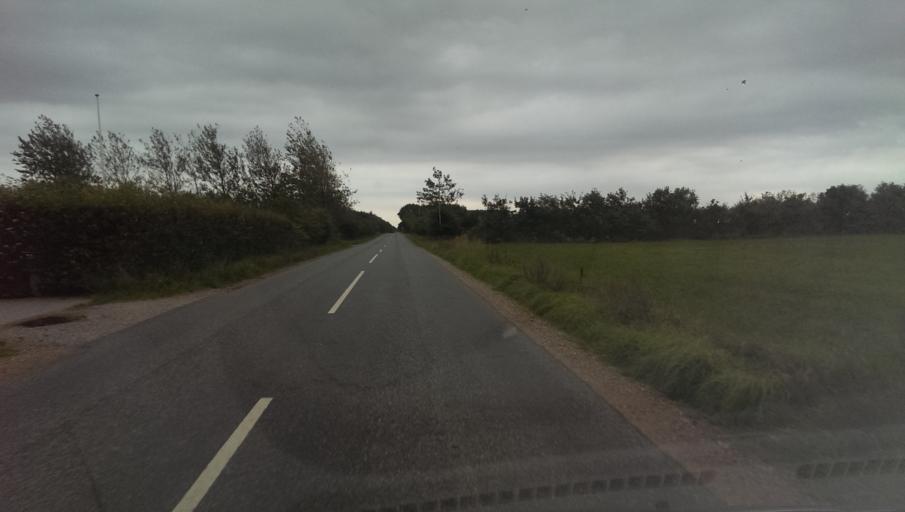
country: DK
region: South Denmark
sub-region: Esbjerg Kommune
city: Tjaereborg
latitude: 55.4859
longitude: 8.5545
